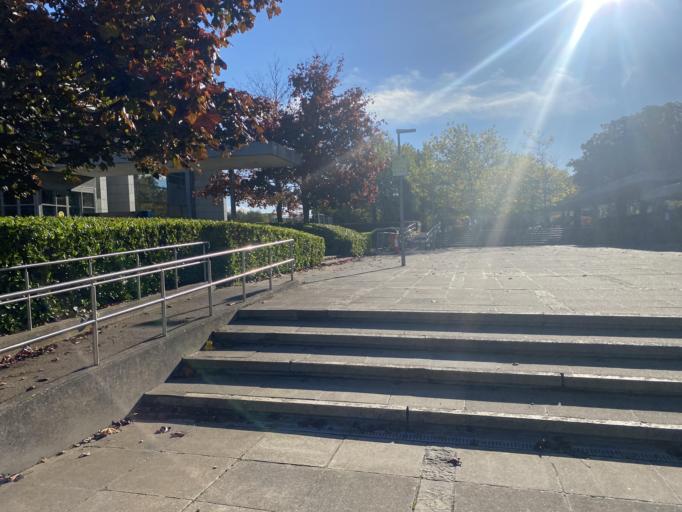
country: IE
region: Leinster
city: Donnybrook
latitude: 53.3062
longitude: -6.2208
